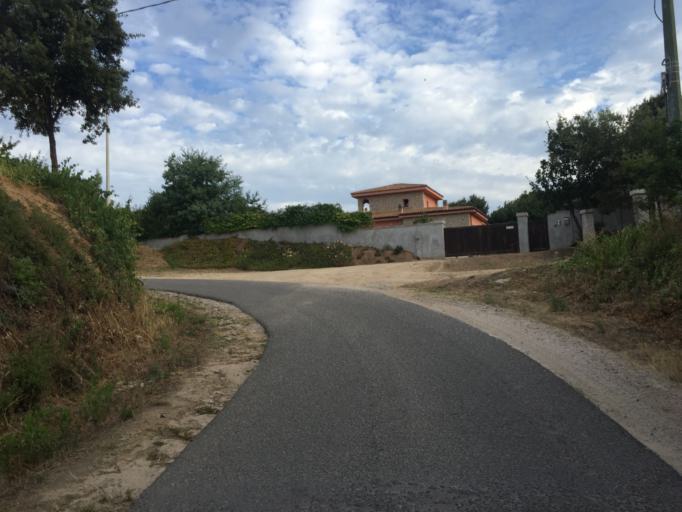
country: IT
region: Sardinia
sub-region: Provincia di Olbia-Tempio
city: Aggius
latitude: 40.9277
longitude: 9.0709
